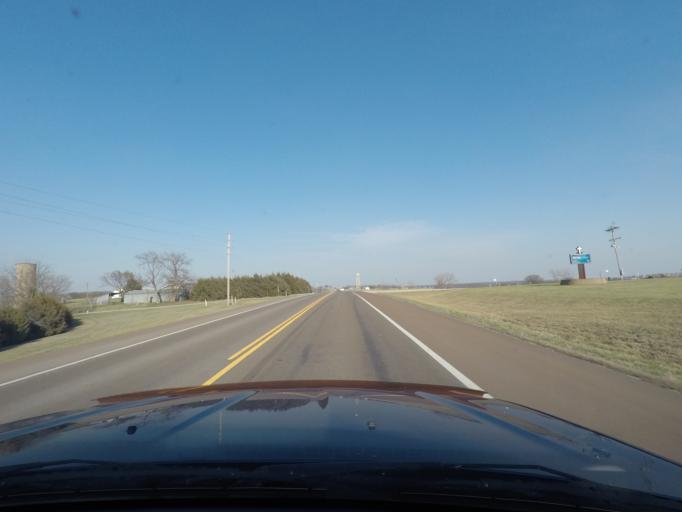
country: US
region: Kansas
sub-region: Douglas County
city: Lawrence
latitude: 39.0004
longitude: -95.3549
